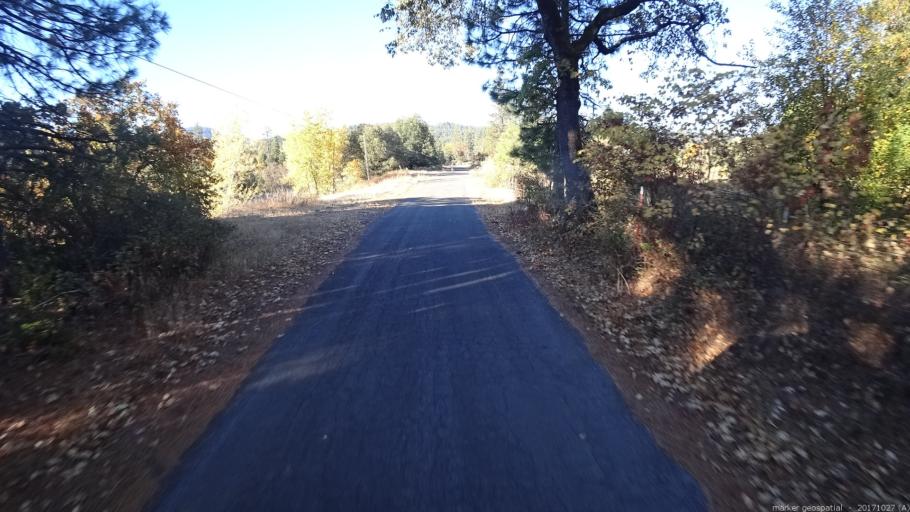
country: US
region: California
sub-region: Shasta County
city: Burney
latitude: 41.0225
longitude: -121.9063
